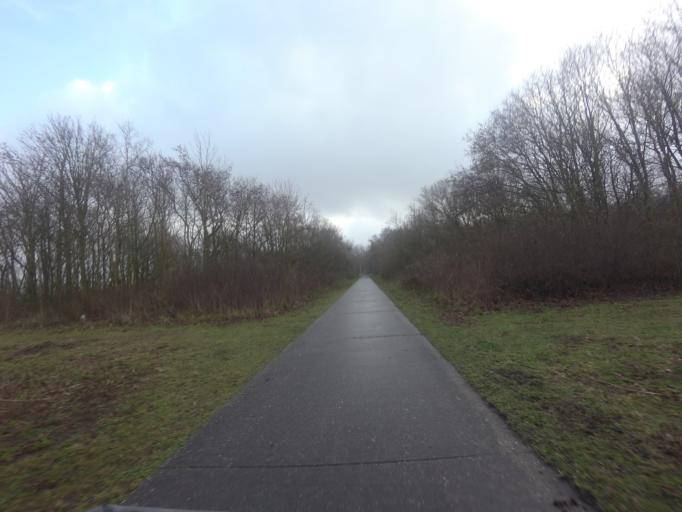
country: NL
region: North Holland
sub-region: Gemeente Texel
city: Den Burg
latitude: 53.1644
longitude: 4.8511
